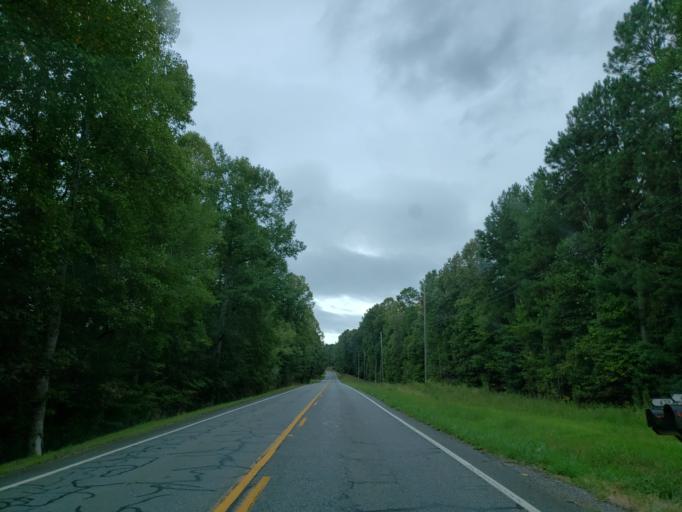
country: US
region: Georgia
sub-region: Gilmer County
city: Ellijay
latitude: 34.6373
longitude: -84.5774
